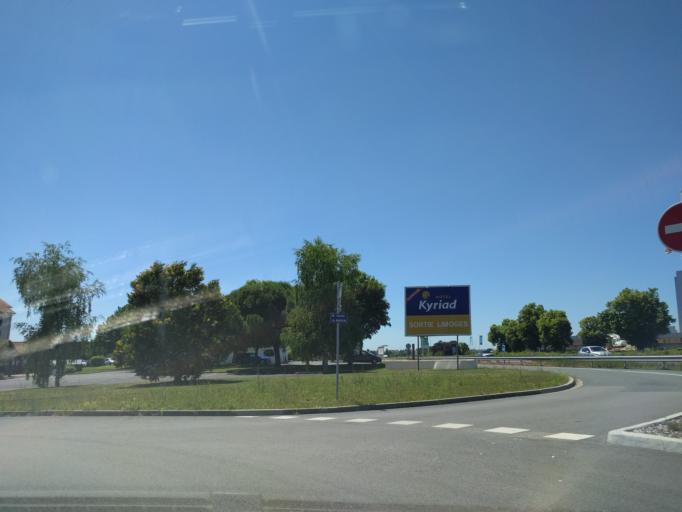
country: FR
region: Poitou-Charentes
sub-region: Departement des Deux-Sevres
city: Chauray
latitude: 46.3399
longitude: -0.4004
